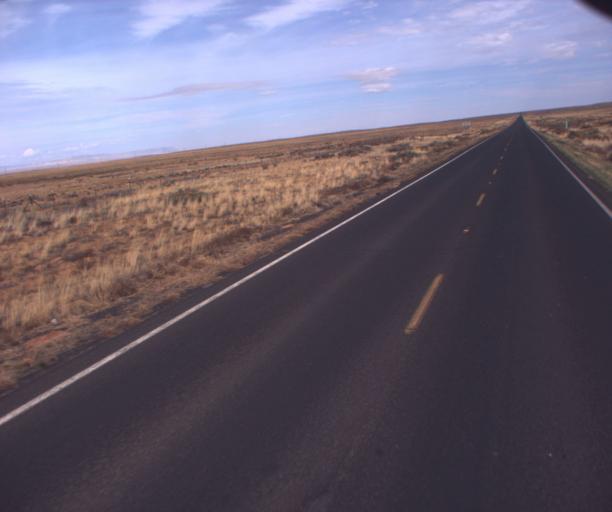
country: US
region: Arizona
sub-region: Apache County
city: Ganado
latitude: 35.8165
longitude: -109.6088
